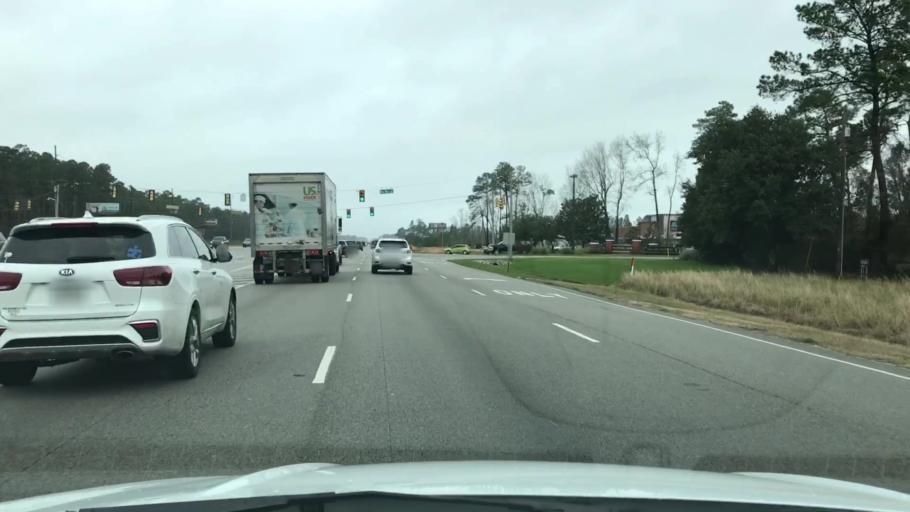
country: US
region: South Carolina
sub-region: Horry County
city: Red Hill
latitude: 33.7817
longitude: -78.9886
